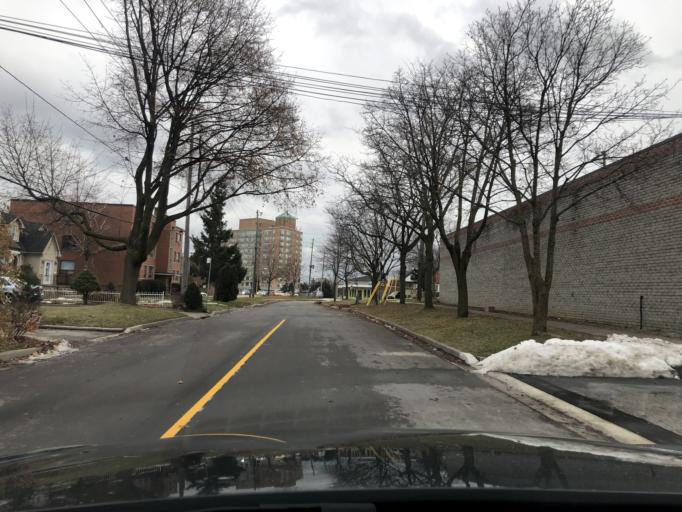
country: CA
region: Ontario
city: Etobicoke
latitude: 43.7017
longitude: -79.5286
